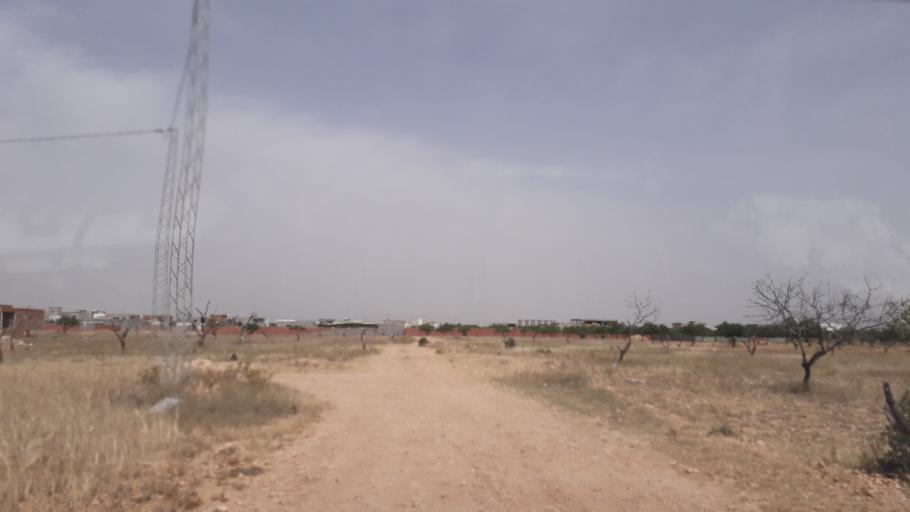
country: TN
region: Safaqis
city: Al Qarmadah
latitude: 34.8393
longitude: 10.7804
